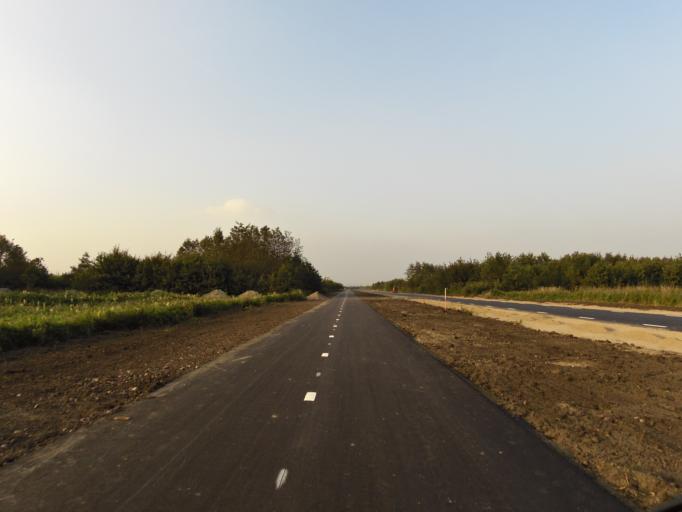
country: NL
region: South Holland
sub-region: Gemeente Rijnwoude
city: Benthuizen
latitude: 52.0657
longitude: 4.5639
